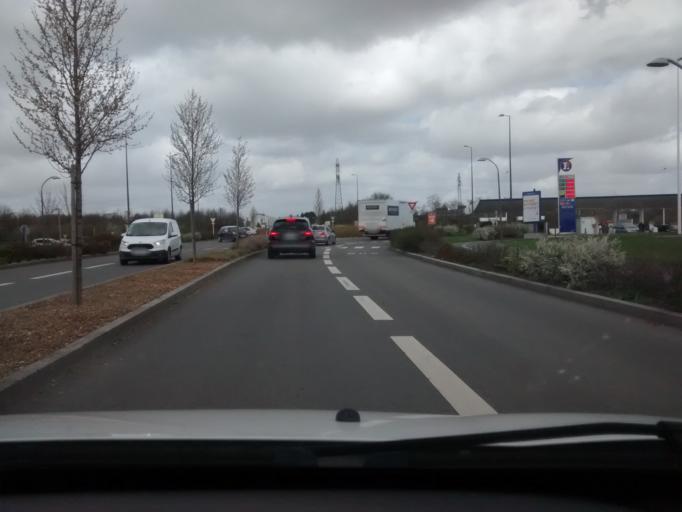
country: FR
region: Brittany
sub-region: Departement d'Ille-et-Vilaine
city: Saint-Gregoire
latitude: 48.1392
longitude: -1.6865
